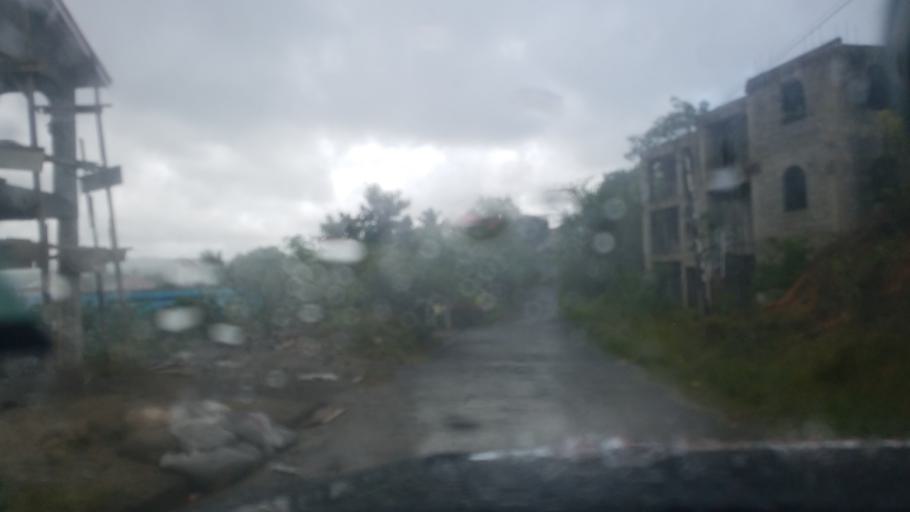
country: LC
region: Laborie Quarter
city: Laborie
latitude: 13.7439
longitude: -60.9678
